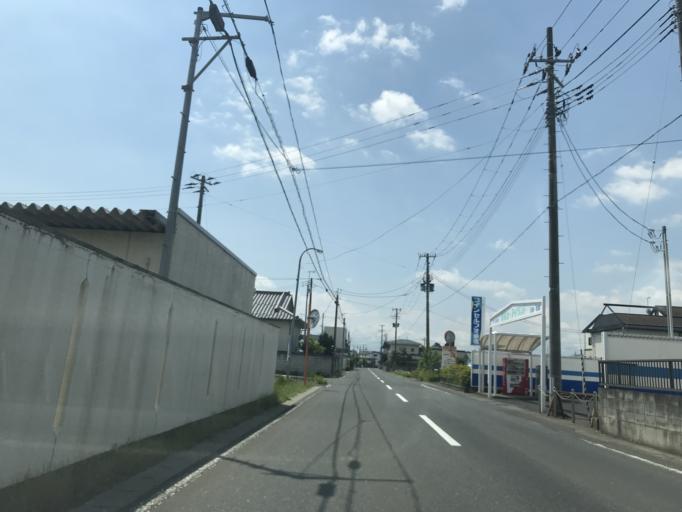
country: JP
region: Miyagi
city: Kogota
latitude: 38.6037
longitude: 141.0223
